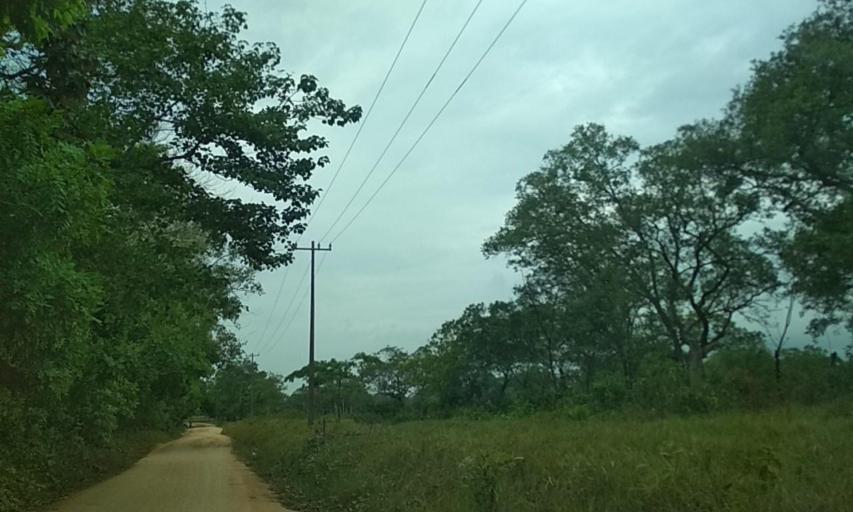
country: MX
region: Veracruz
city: Las Choapas
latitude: 17.8903
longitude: -94.1206
